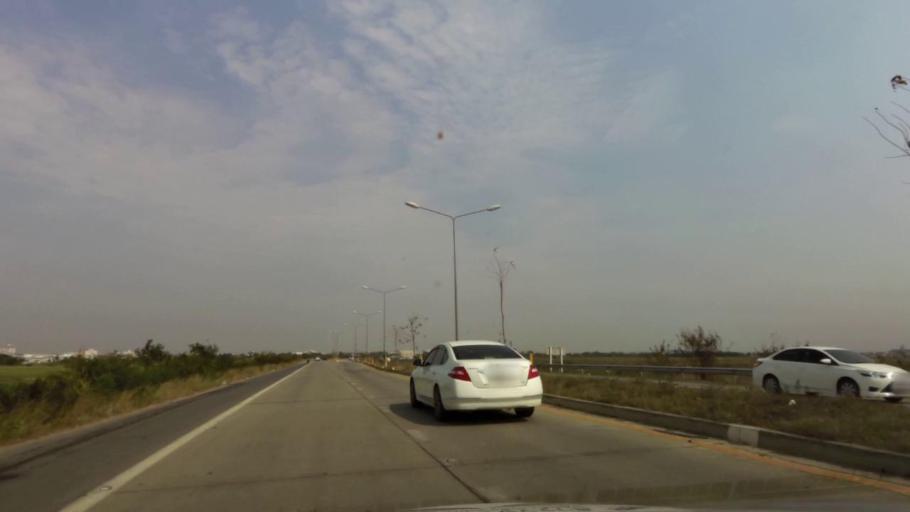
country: TH
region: Phra Nakhon Si Ayutthaya
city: Phra Nakhon Si Ayutthaya
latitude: 14.3316
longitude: 100.5906
